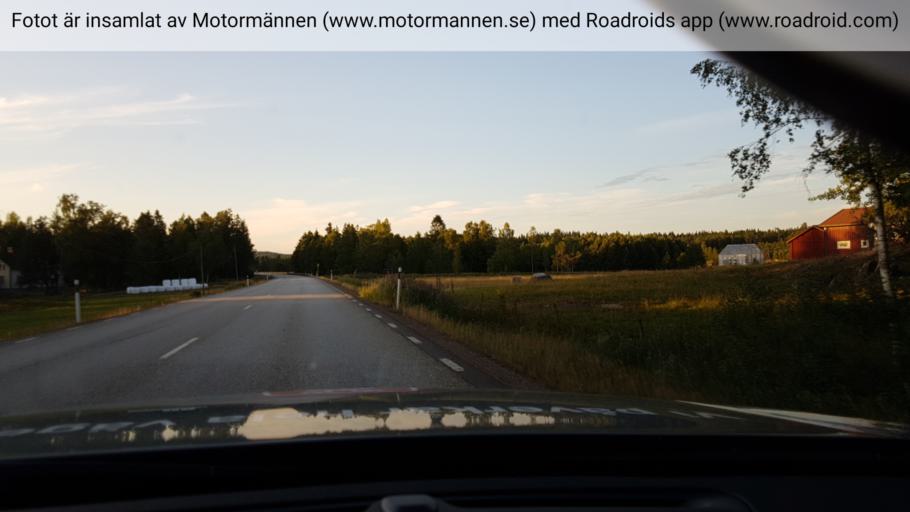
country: SE
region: Vaermland
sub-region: Storfors Kommun
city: Storfors
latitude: 59.4808
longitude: 14.3286
